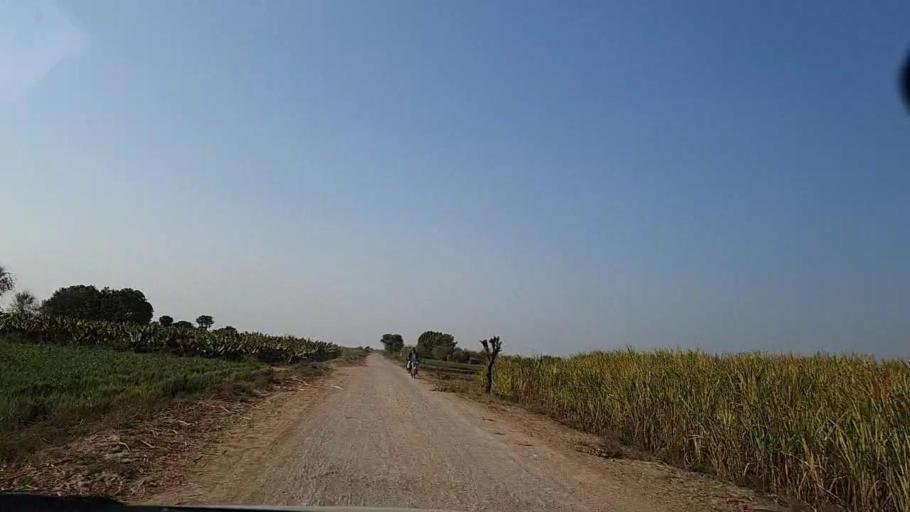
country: PK
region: Sindh
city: Mirwah Gorchani
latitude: 25.2272
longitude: 68.9855
